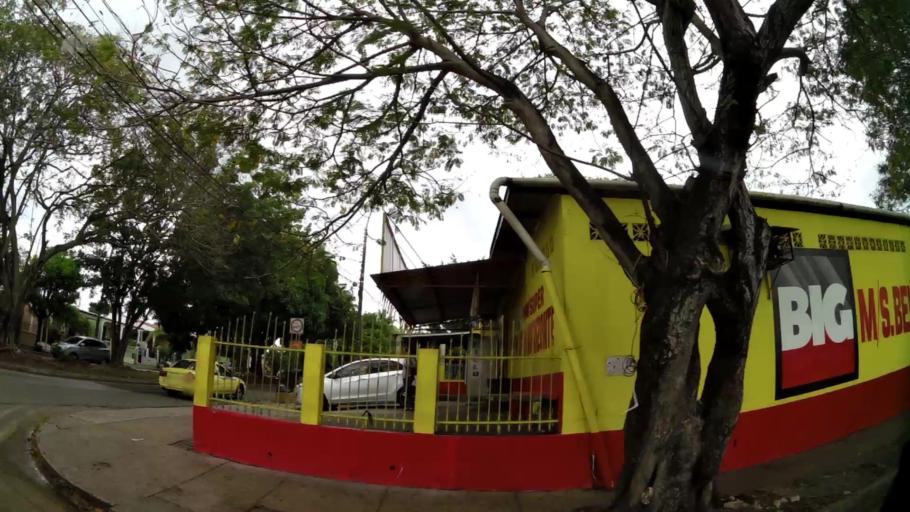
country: PA
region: Panama
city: Tocumen
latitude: 9.0539
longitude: -79.4105
